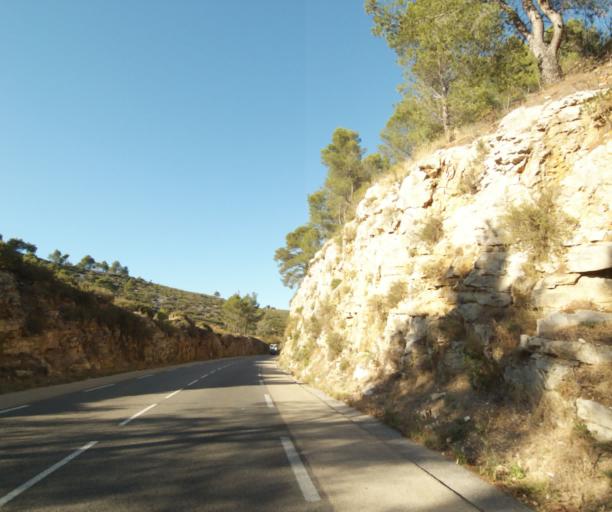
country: FR
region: Provence-Alpes-Cote d'Azur
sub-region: Departement des Bouches-du-Rhone
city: Cassis
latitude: 43.2088
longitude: 5.5806
